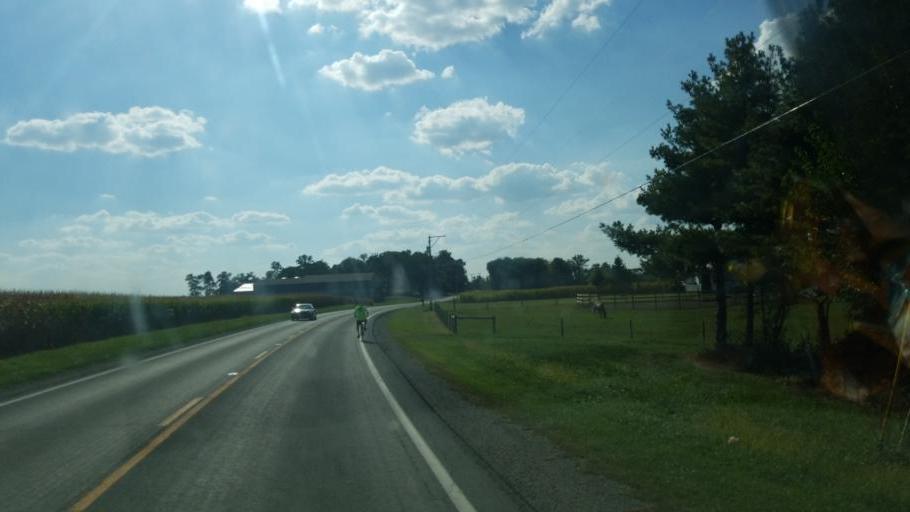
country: US
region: Ohio
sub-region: Wyandot County
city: Upper Sandusky
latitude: 40.7652
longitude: -83.3267
